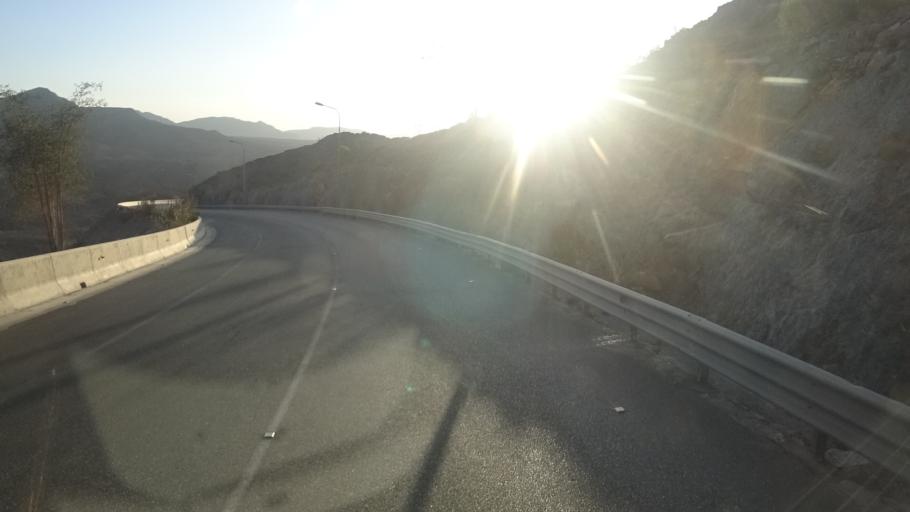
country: OM
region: Muhafazat ad Dakhiliyah
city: Izki
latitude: 23.0662
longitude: 57.7213
